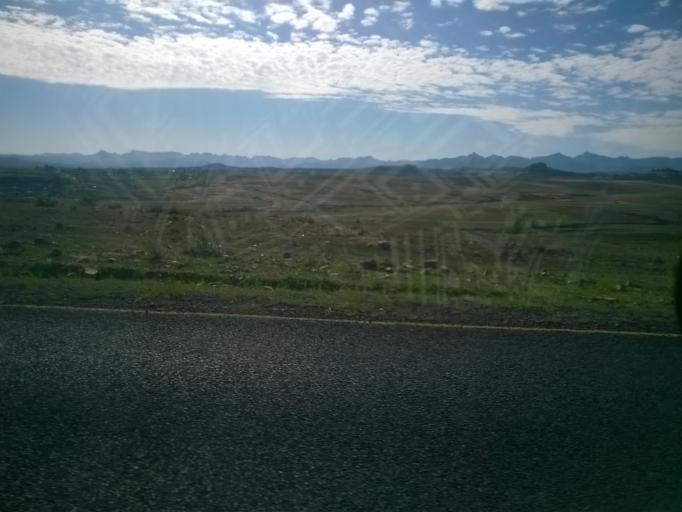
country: LS
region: Berea
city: Teyateyaneng
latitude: -29.0943
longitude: 27.8553
